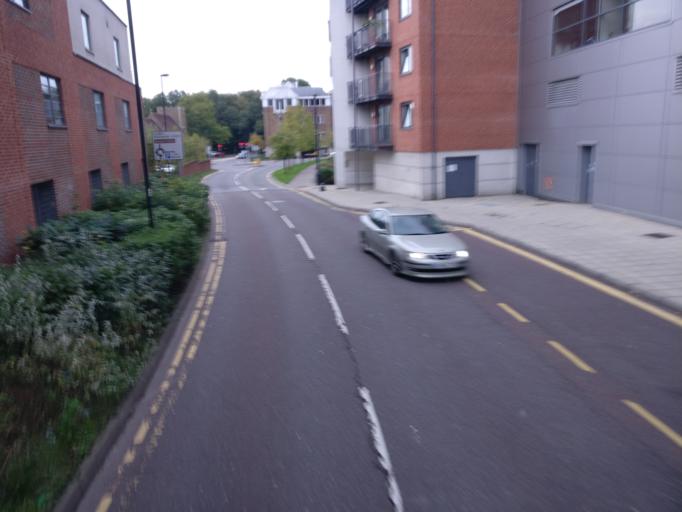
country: GB
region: England
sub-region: Surrey
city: Camberley
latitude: 51.3372
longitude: -0.7492
